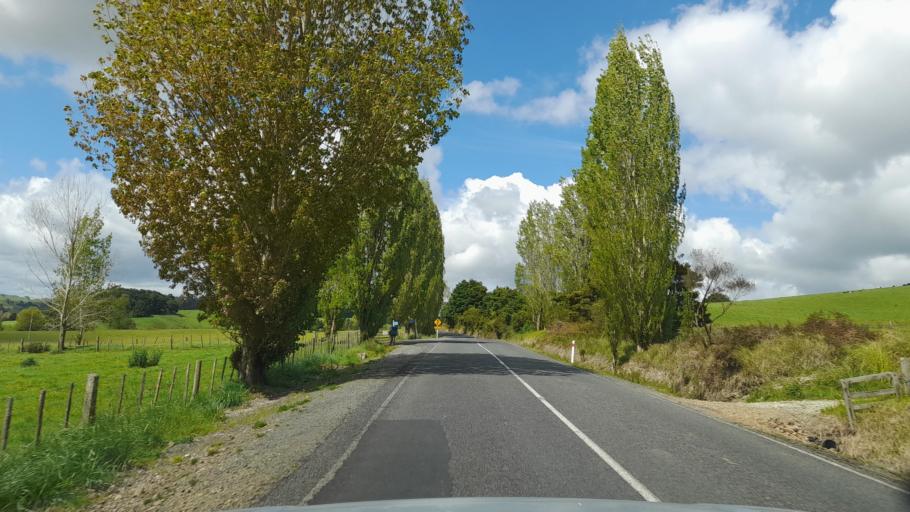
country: NZ
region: Northland
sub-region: Whangarei
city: Maungatapere
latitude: -35.6268
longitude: 174.0975
